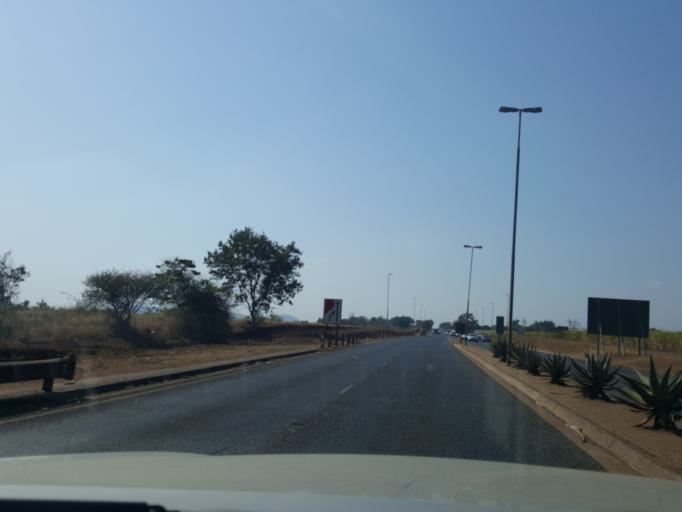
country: SZ
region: Hhohho
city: Ntfonjeni
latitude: -25.4965
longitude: 31.5155
